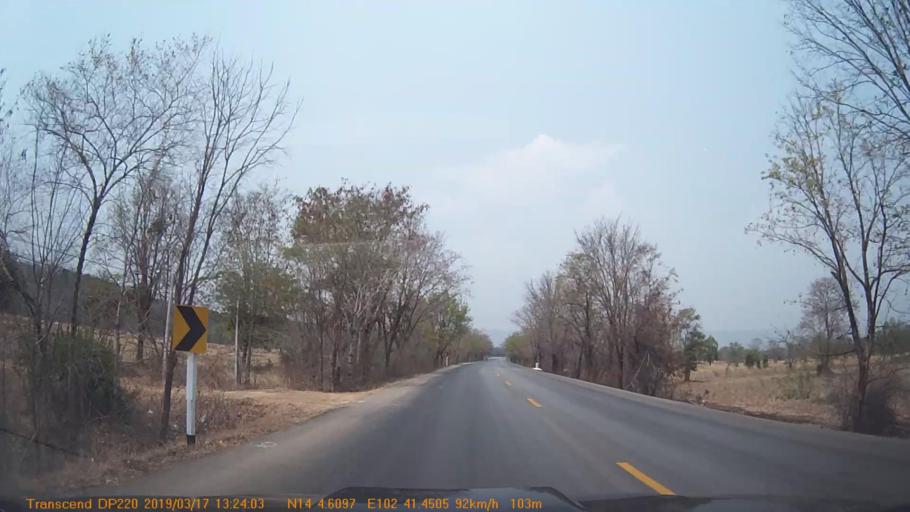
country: TH
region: Sa Kaeo
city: Ta Phraya
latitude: 14.0772
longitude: 102.6908
